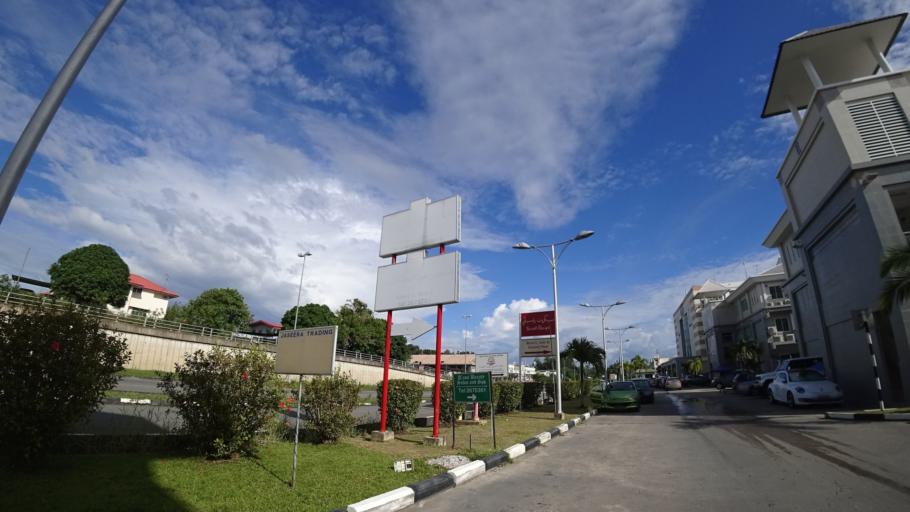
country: BN
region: Brunei and Muara
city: Bandar Seri Begawan
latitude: 4.8904
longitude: 114.8569
